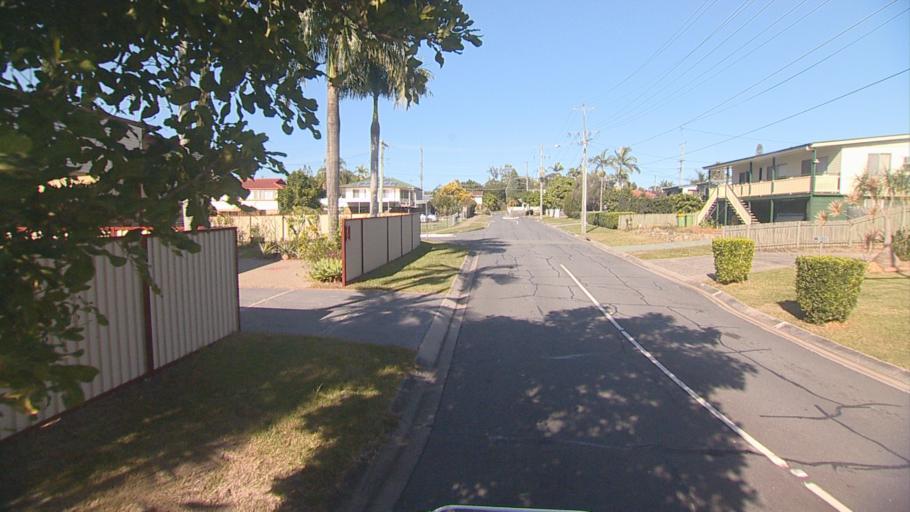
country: AU
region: Queensland
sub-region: Logan
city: Logan City
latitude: -27.6315
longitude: 153.1238
